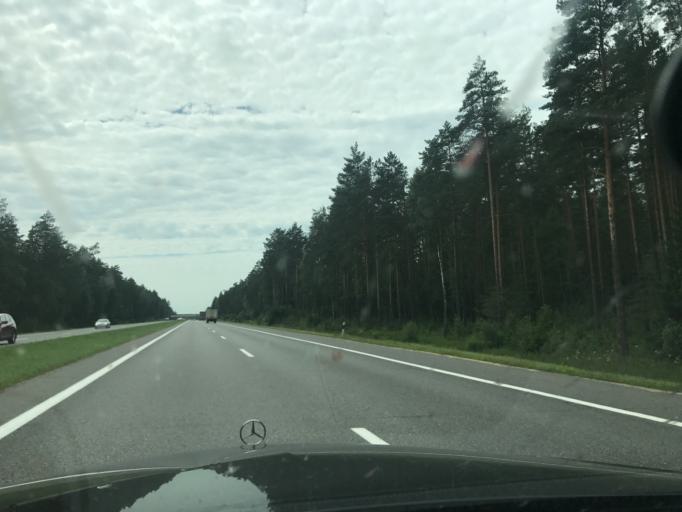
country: BY
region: Minsk
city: Zamostochcha
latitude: 53.9001
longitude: 27.9454
